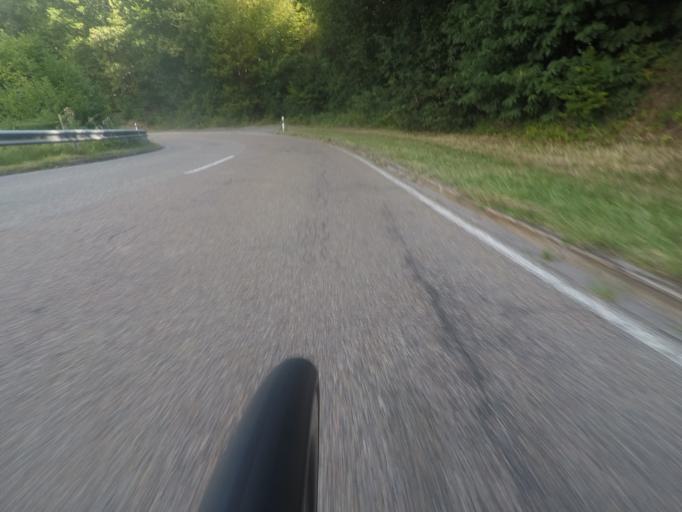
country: DE
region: Baden-Wuerttemberg
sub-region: Karlsruhe Region
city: Loffenau
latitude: 48.7756
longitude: 8.4004
